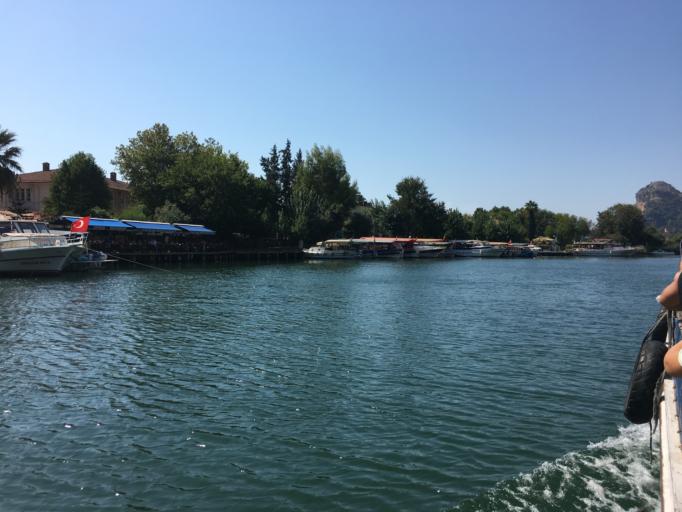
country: TR
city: Dalyan
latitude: 36.8337
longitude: 28.6394
